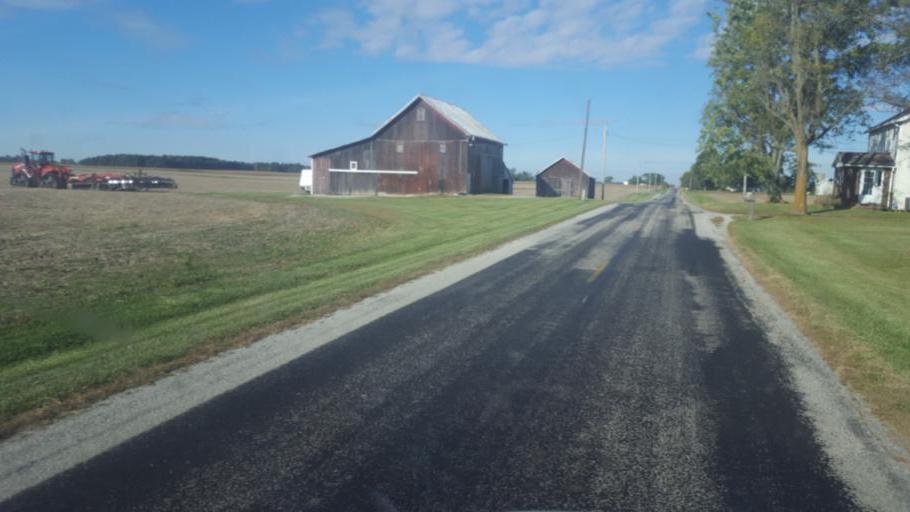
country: US
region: Ohio
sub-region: Crawford County
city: Bucyrus
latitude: 40.6886
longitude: -83.0327
